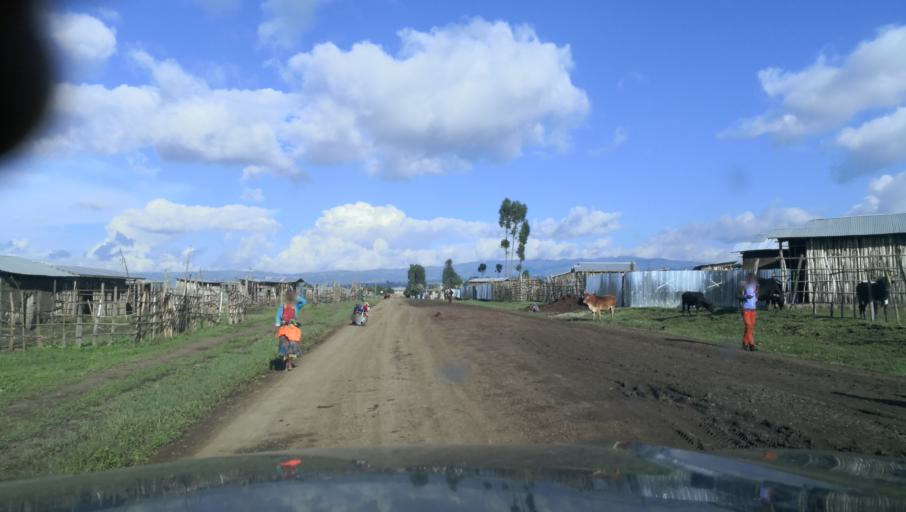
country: ET
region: Oromiya
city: Tulu Bolo
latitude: 8.4752
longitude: 38.2423
